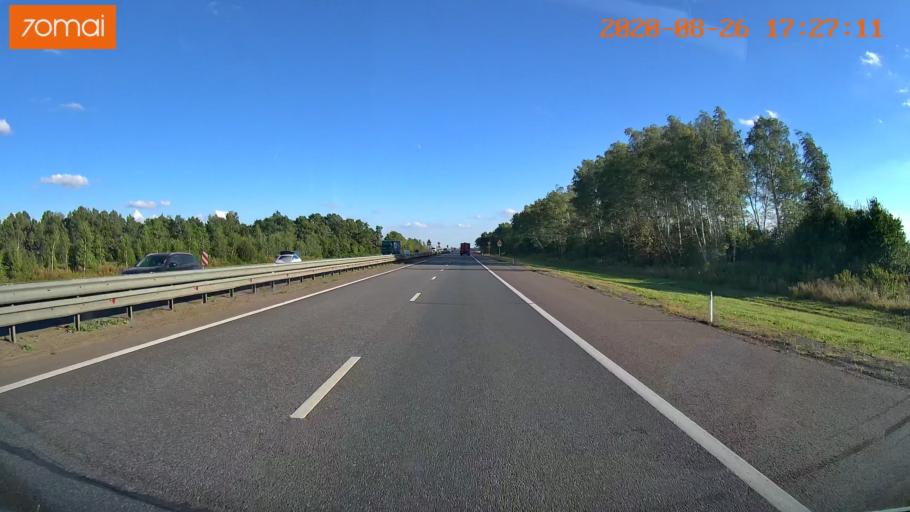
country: RU
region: Tula
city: Kazachka
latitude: 53.4762
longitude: 38.1228
